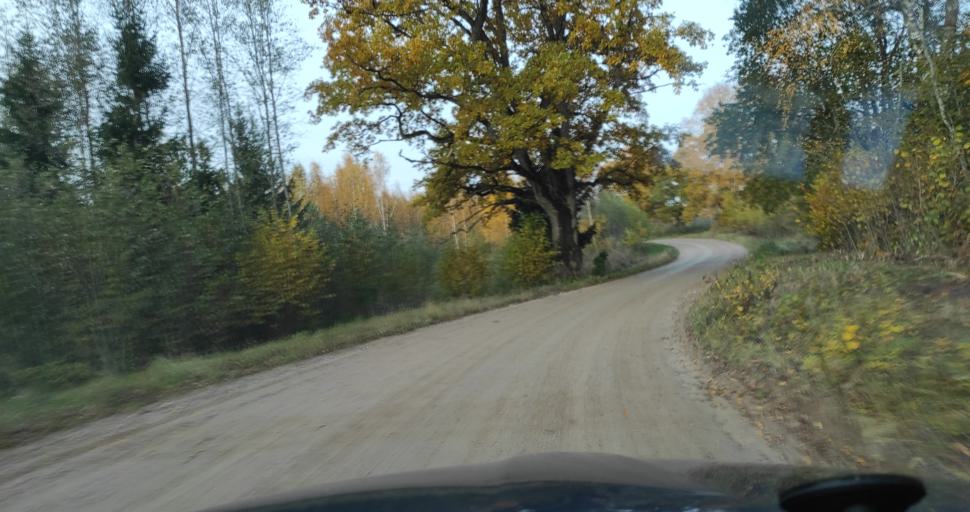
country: LV
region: Vainode
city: Vainode
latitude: 56.6256
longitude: 21.8164
